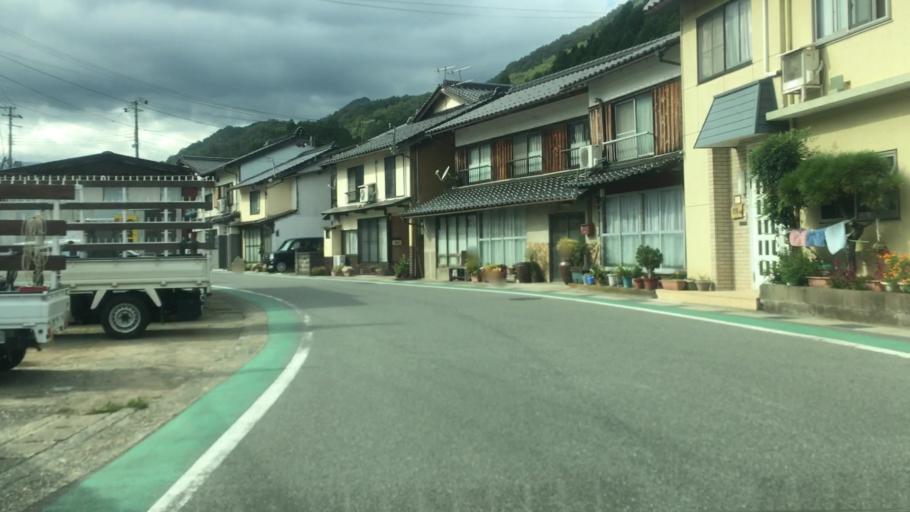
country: JP
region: Hyogo
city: Toyooka
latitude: 35.4079
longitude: 134.7590
